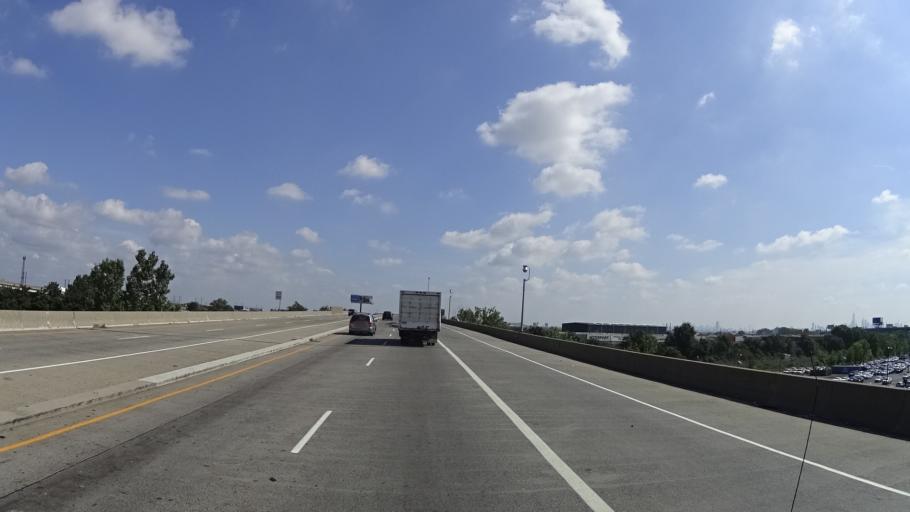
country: US
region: New Jersey
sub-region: Essex County
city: Newark
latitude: 40.7118
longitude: -74.1571
